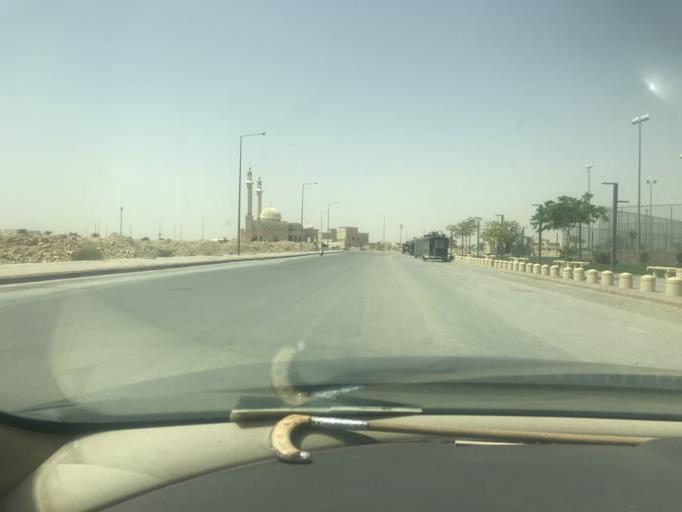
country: SA
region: Ar Riyad
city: Riyadh
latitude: 24.7883
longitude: 46.5804
